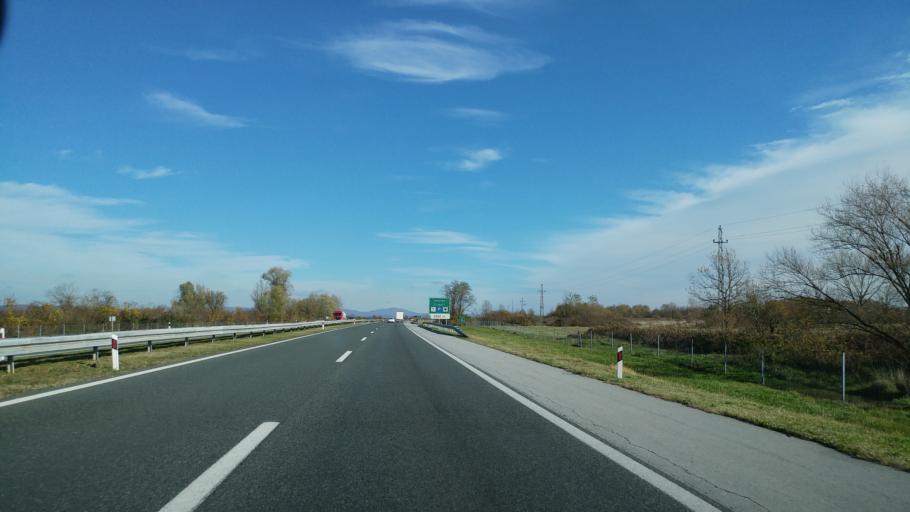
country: HR
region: Brodsko-Posavska
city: Okucani
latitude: 45.2324
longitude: 17.2560
